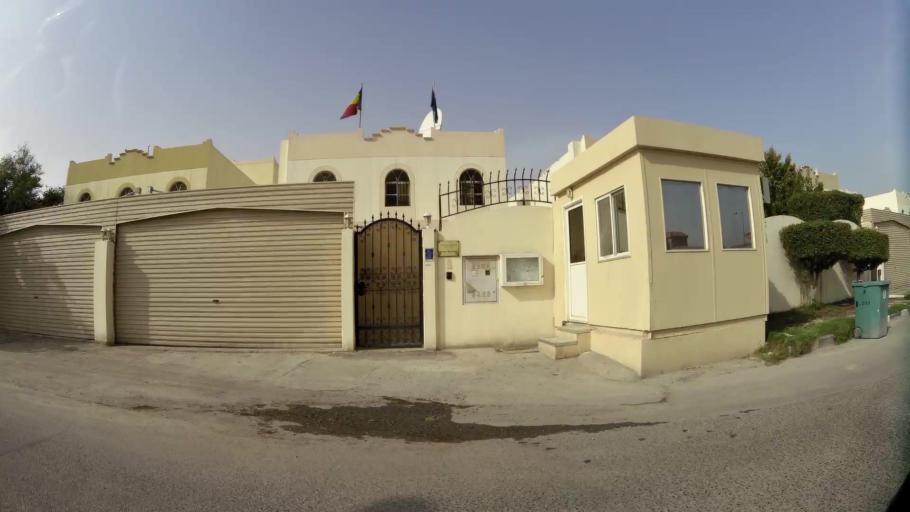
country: QA
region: Baladiyat ad Dawhah
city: Doha
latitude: 25.3225
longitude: 51.5030
